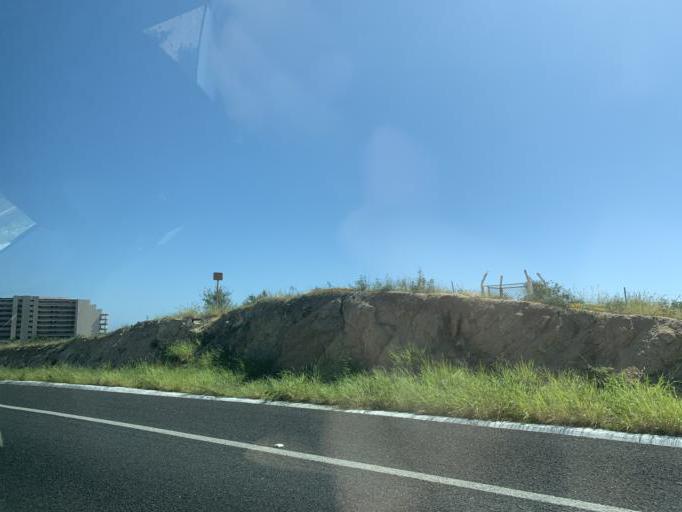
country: MX
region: Baja California Sur
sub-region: Los Cabos
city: San Jose del Cabo
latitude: 22.9663
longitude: -109.7966
